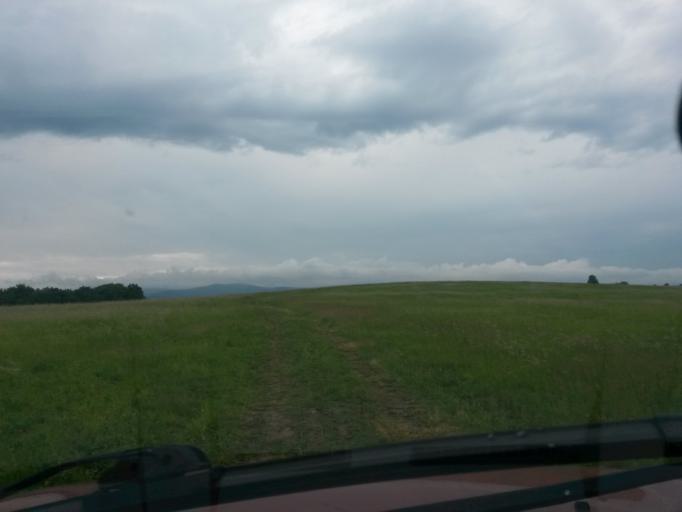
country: SK
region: Kosicky
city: Kosice
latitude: 48.7036
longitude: 21.1632
